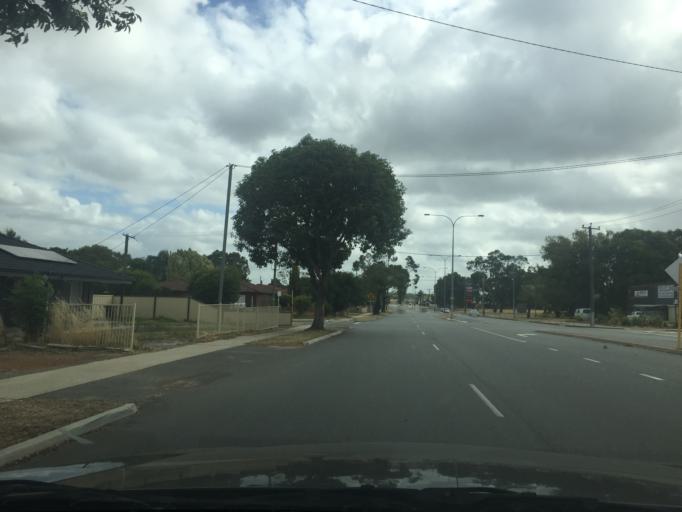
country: AU
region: Western Australia
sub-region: Gosnells
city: Maddington
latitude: -32.0520
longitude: 115.9833
